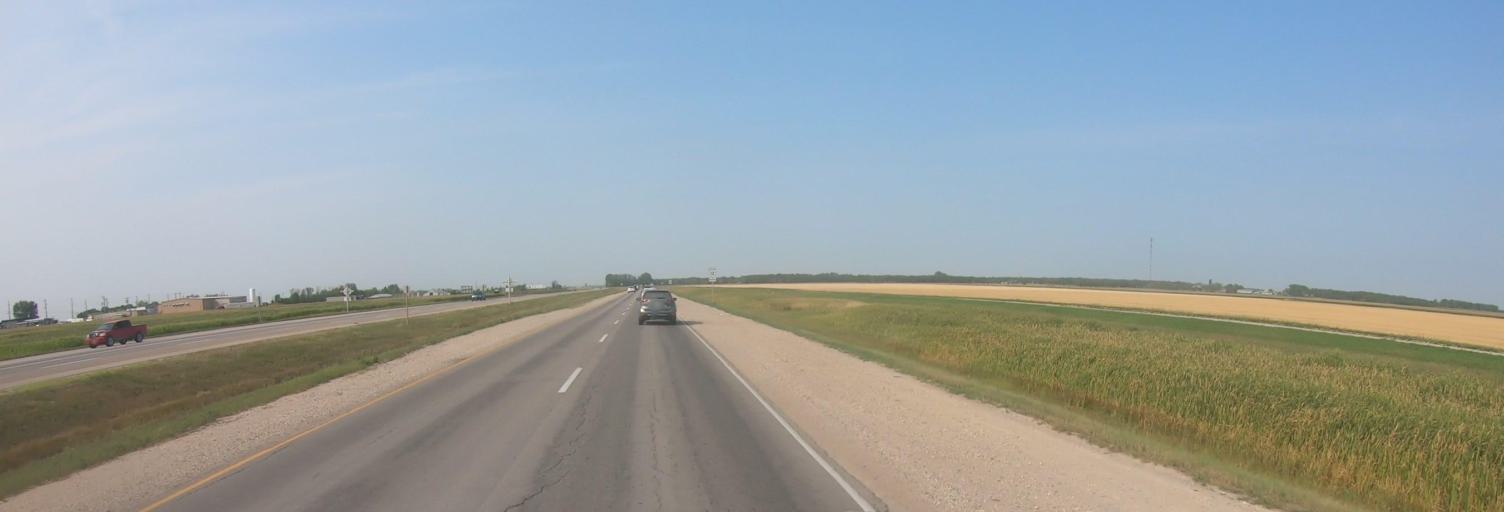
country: CA
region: Manitoba
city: Steinbach
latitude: 49.6048
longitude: -96.6823
